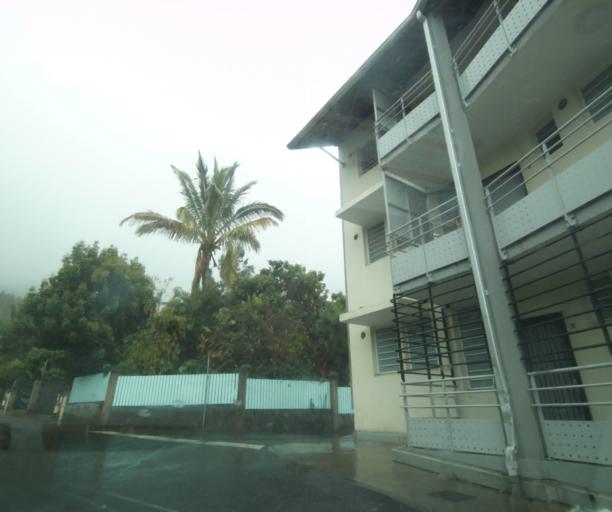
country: RE
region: Reunion
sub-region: Reunion
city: La Possession
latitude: -20.9809
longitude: 55.3404
